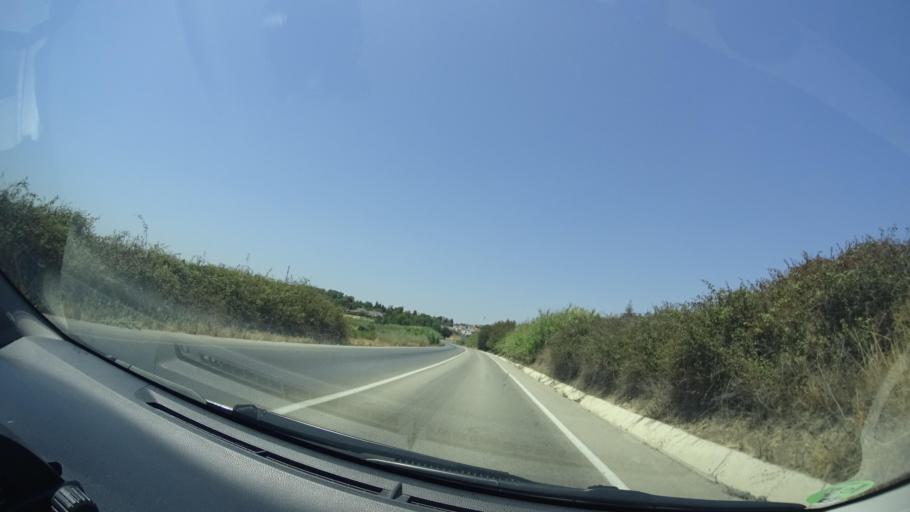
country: ES
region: Andalusia
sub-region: Provincia de Cadiz
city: Jerez de la Frontera
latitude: 36.6574
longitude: -6.0969
